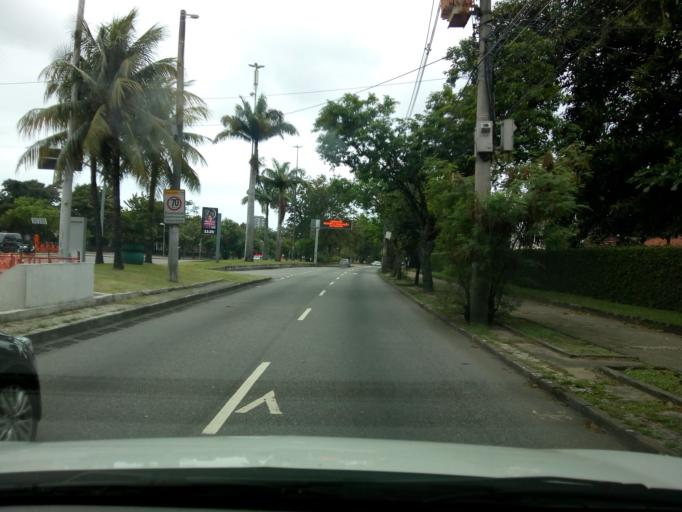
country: BR
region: Rio de Janeiro
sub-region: Rio De Janeiro
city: Rio de Janeiro
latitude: -22.9718
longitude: -43.2177
